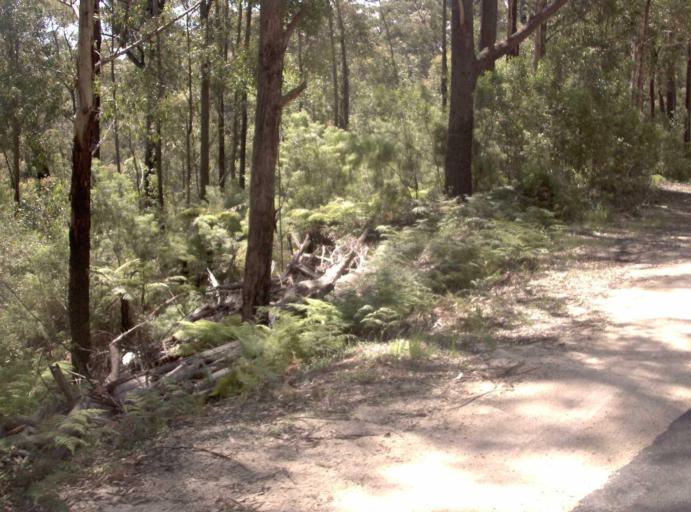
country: AU
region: New South Wales
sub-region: Bombala
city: Bombala
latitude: -37.5913
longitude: 148.9898
